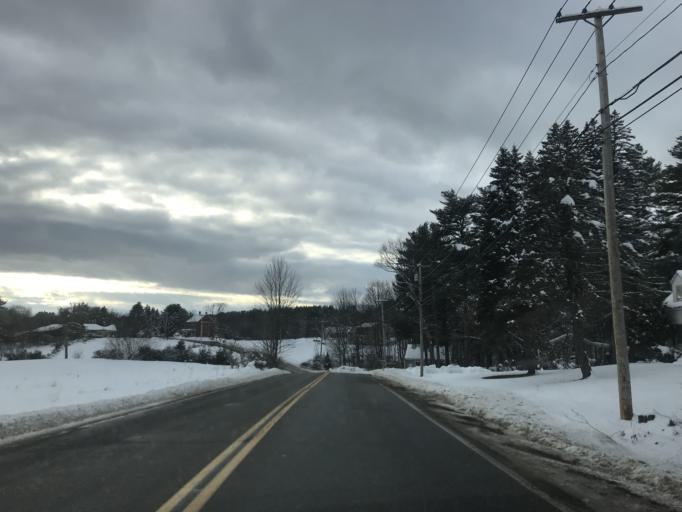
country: US
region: Maine
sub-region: Cumberland County
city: Westbrook
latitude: 43.7179
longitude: -70.3268
